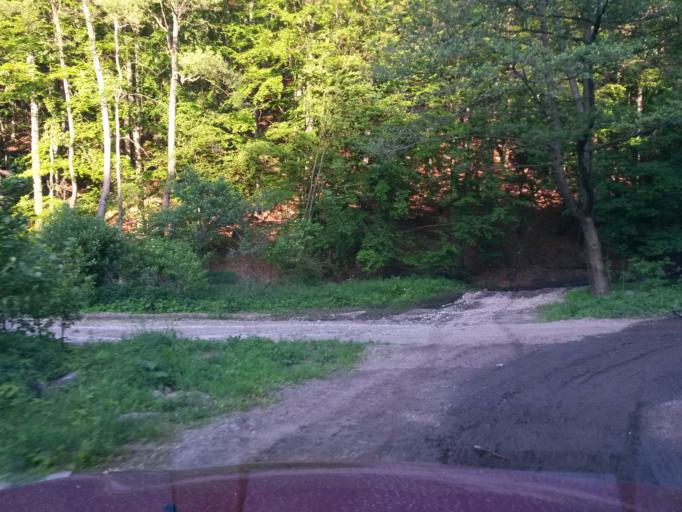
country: SK
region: Kosicky
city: Moldava nad Bodvou
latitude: 48.7394
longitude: 21.0640
